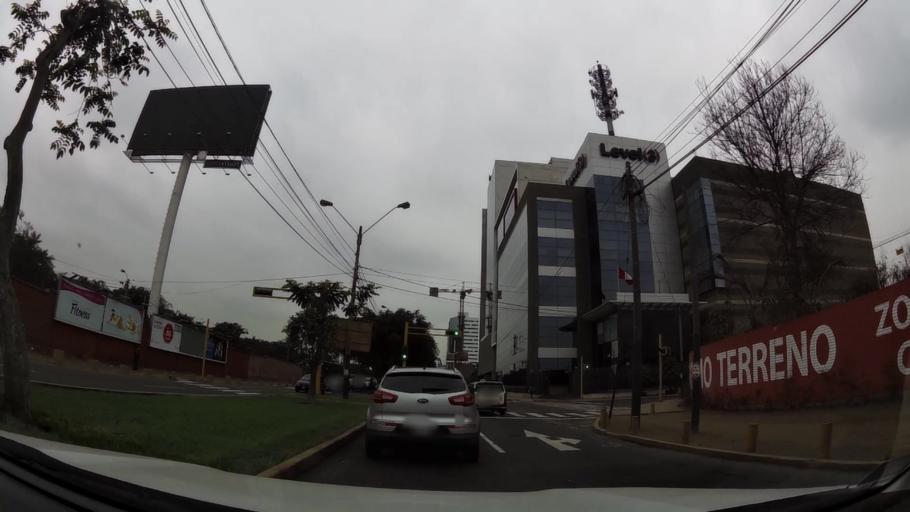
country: PE
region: Lima
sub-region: Lima
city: La Molina
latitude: -12.0895
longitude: -76.9736
